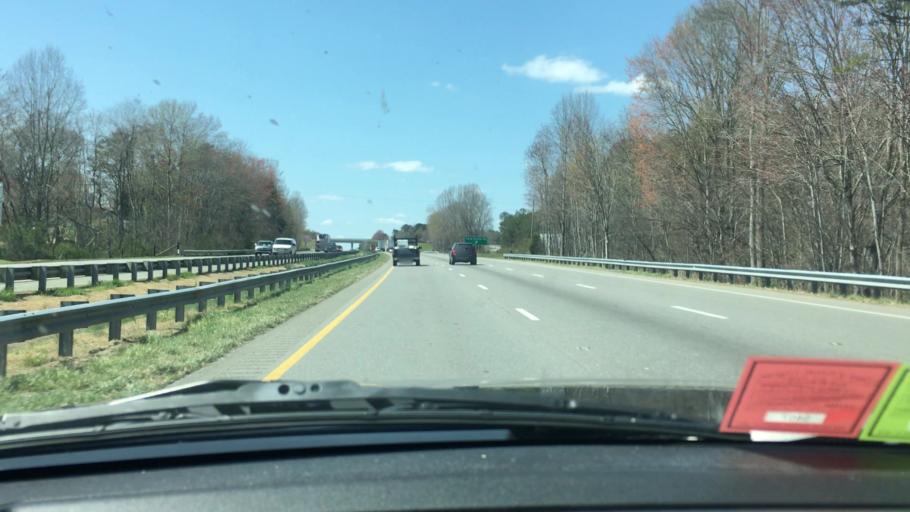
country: US
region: North Carolina
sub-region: Surry County
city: Pilot Mountain
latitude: 36.4044
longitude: -80.4948
